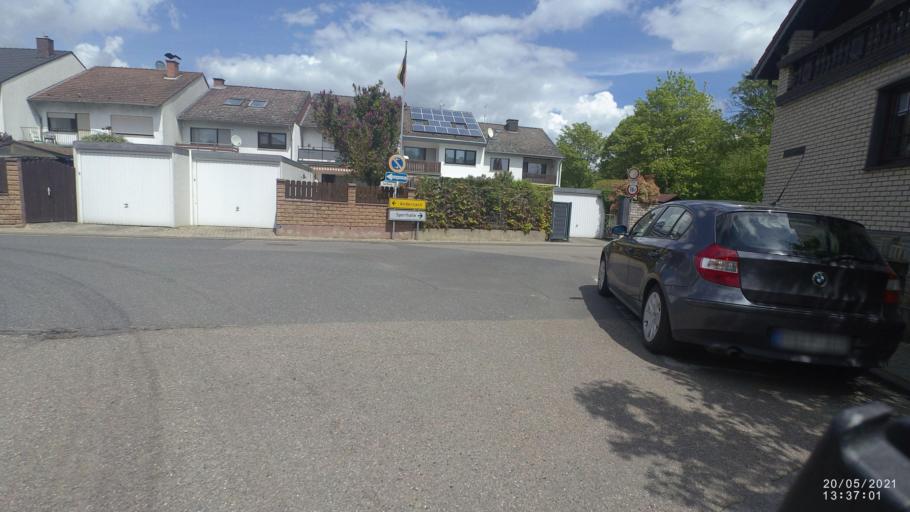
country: DE
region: Rheinland-Pfalz
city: Saffig
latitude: 50.4022
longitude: 7.4158
